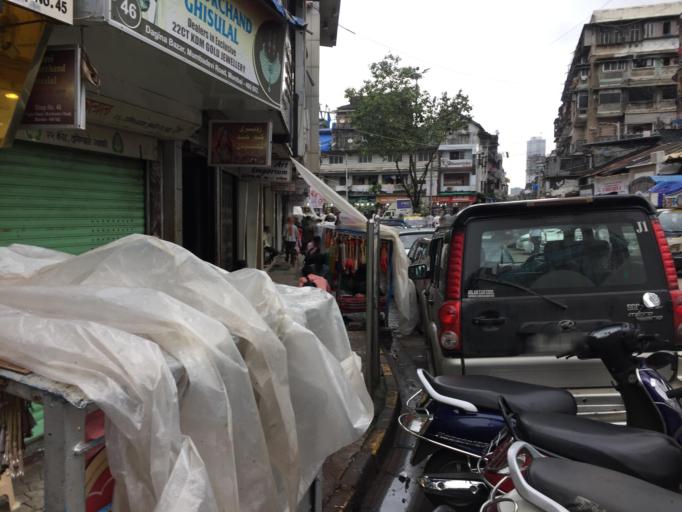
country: IN
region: Maharashtra
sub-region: Mumbai Suburban
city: Mumbai
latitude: 18.9530
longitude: 72.8313
